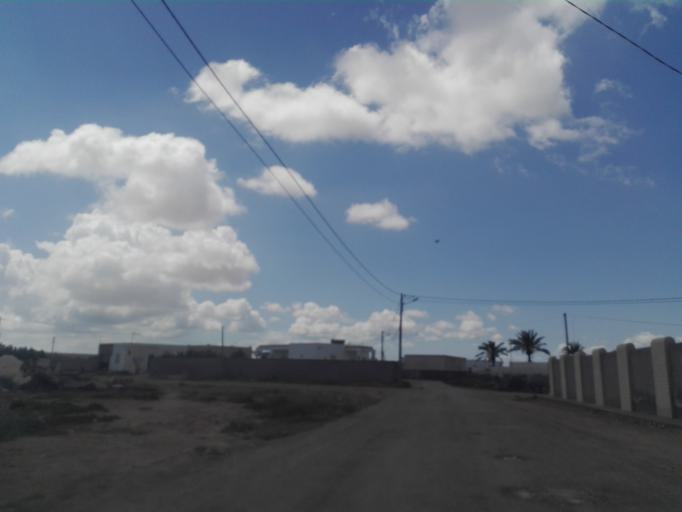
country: TN
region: Safaqis
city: Jabinyanah
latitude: 34.8227
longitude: 11.2534
